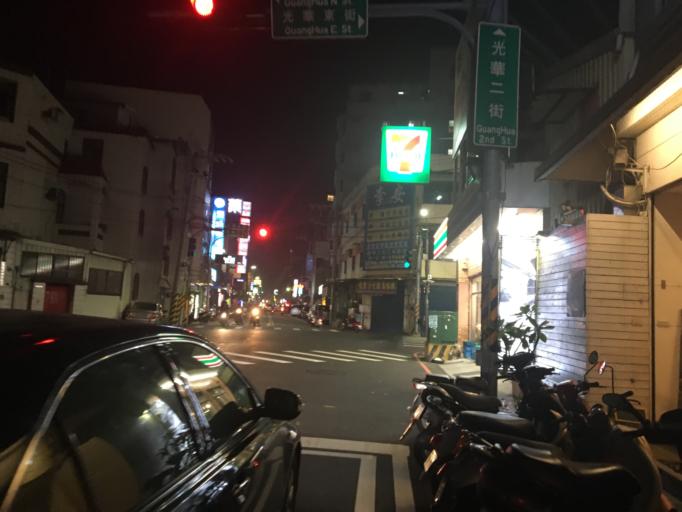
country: TW
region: Taiwan
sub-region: Hsinchu
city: Hsinchu
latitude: 24.8177
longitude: 120.9744
